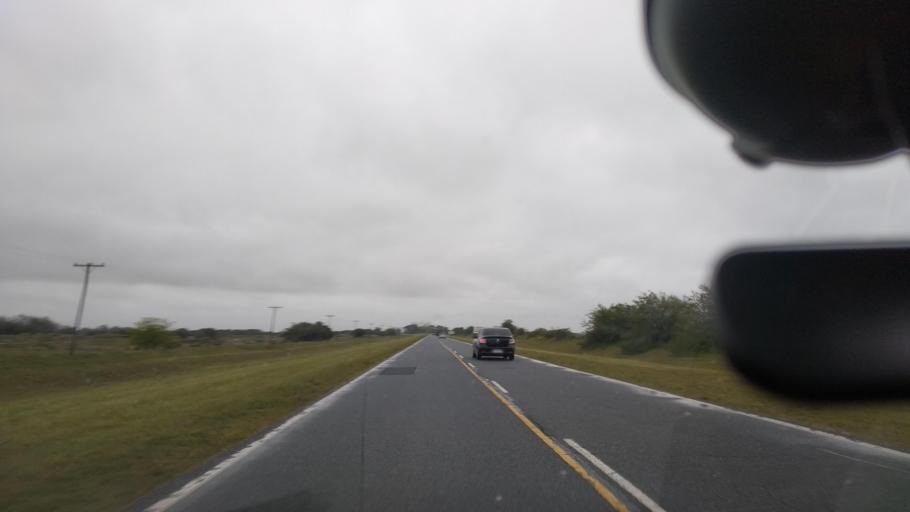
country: AR
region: Buenos Aires
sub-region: Partido de Castelli
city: Castelli
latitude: -35.9630
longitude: -57.4482
